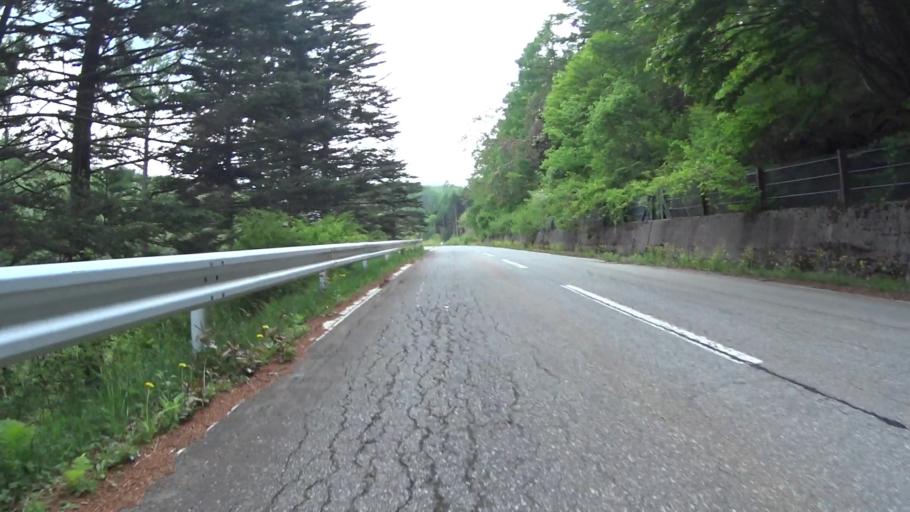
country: JP
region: Nagano
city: Saku
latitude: 36.0873
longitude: 138.3879
